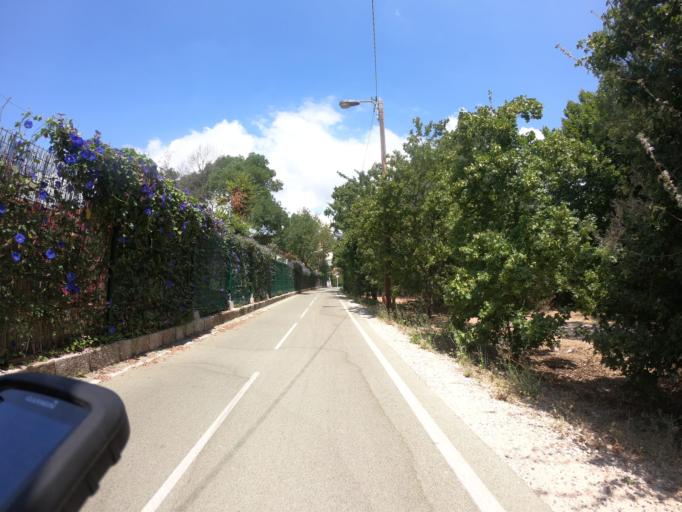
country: FR
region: Provence-Alpes-Cote d'Azur
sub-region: Departement du Var
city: La Valette-du-Var
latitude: 43.1209
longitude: 5.9680
